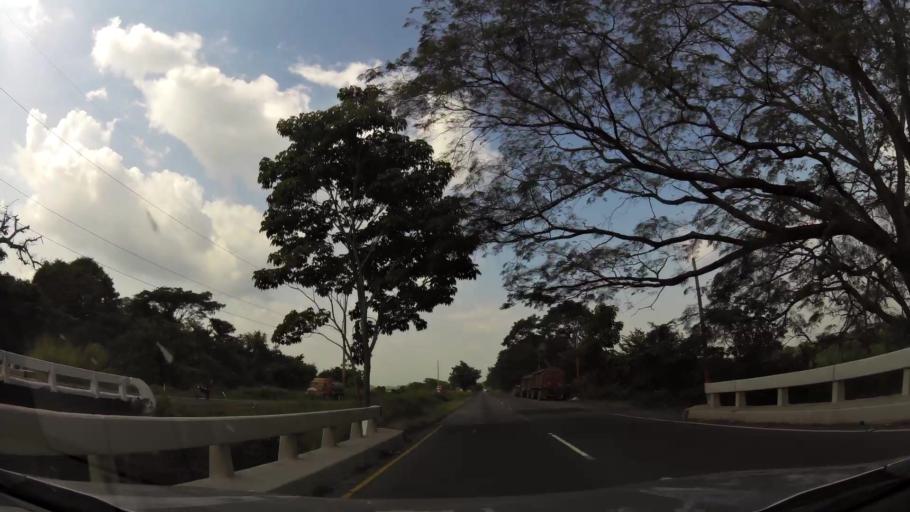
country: GT
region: Escuintla
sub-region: Municipio de Masagua
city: Masagua
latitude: 14.0774
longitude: -90.7777
